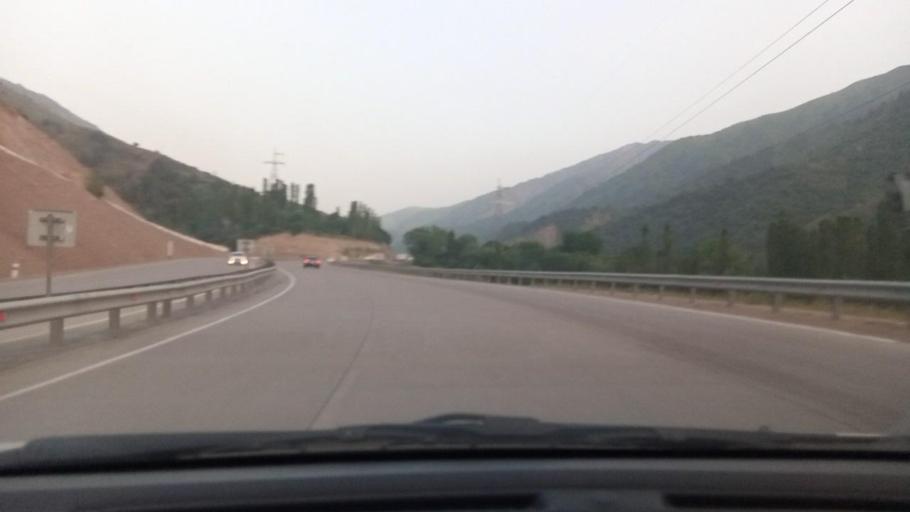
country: UZ
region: Toshkent
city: Angren
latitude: 41.1456
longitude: 70.4464
